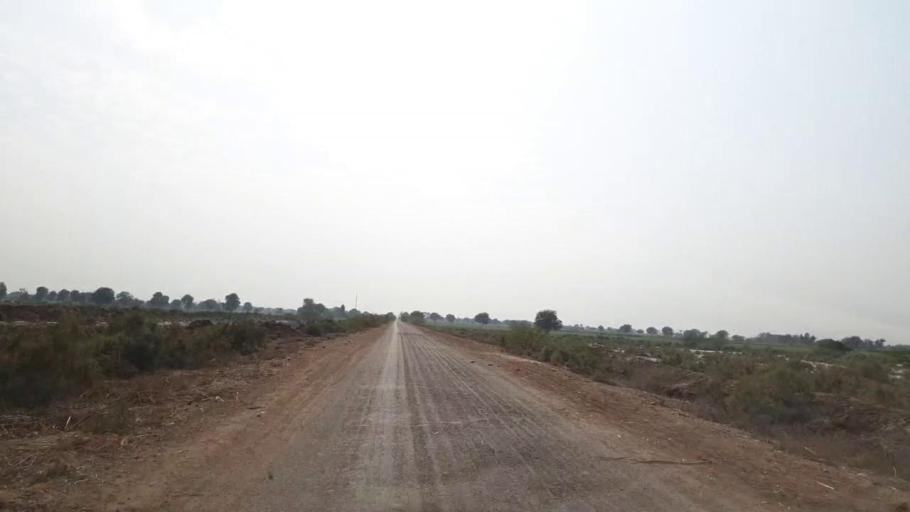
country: PK
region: Sindh
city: Mirpur Khas
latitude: 25.5502
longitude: 69.1695
